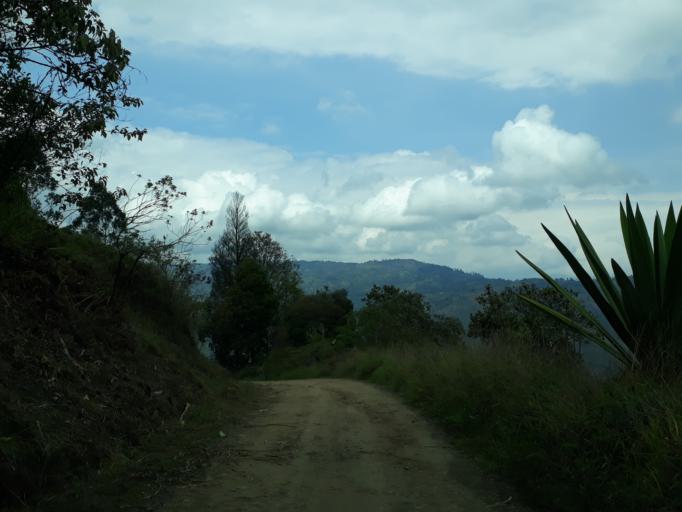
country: CO
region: Cundinamarca
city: Manta
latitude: 5.0172
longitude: -73.5441
